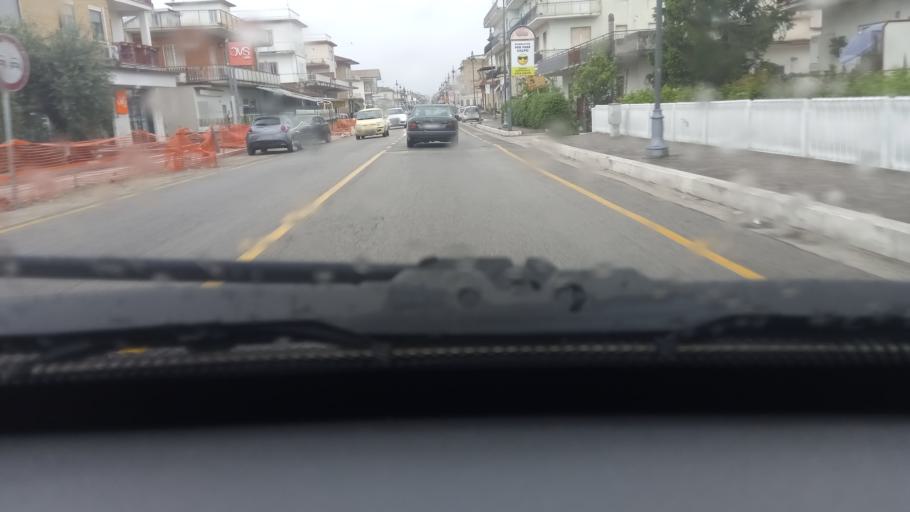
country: IT
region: Latium
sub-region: Provincia di Latina
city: Minturno
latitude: 41.2528
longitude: 13.7240
